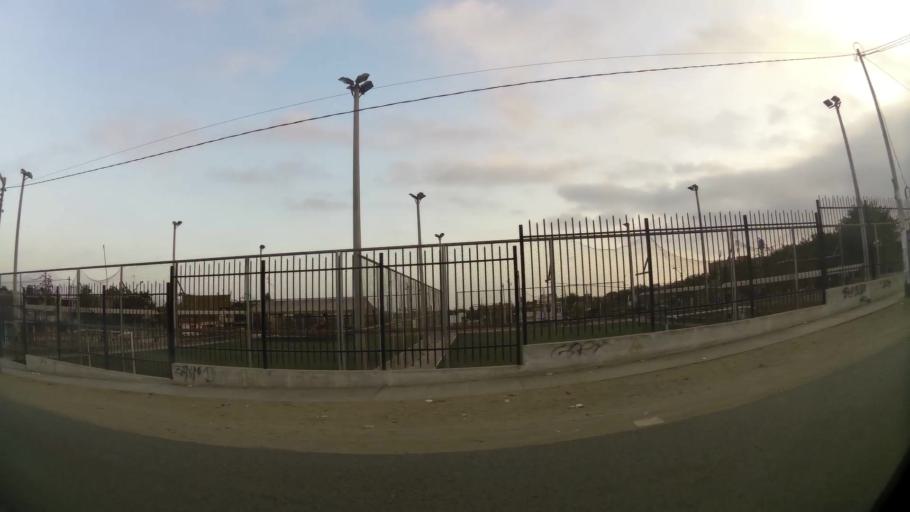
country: PE
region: La Libertad
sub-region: Provincia de Trujillo
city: El Porvenir
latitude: -8.0712
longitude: -79.0059
